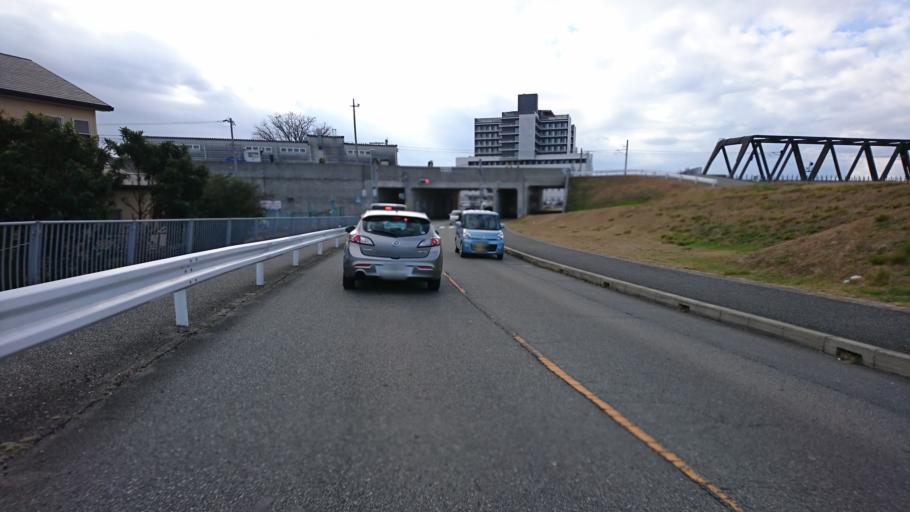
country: JP
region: Hyogo
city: Kakogawacho-honmachi
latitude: 34.7726
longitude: 134.8358
